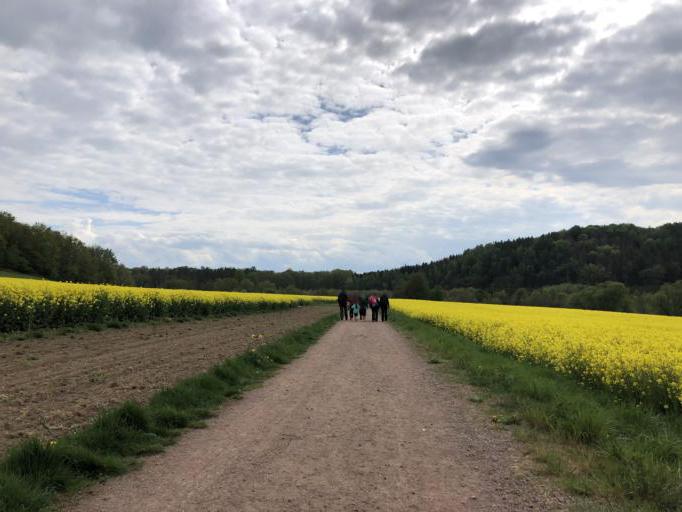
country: DE
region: Saxony
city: Wechselburg
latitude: 51.0148
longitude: 12.7811
